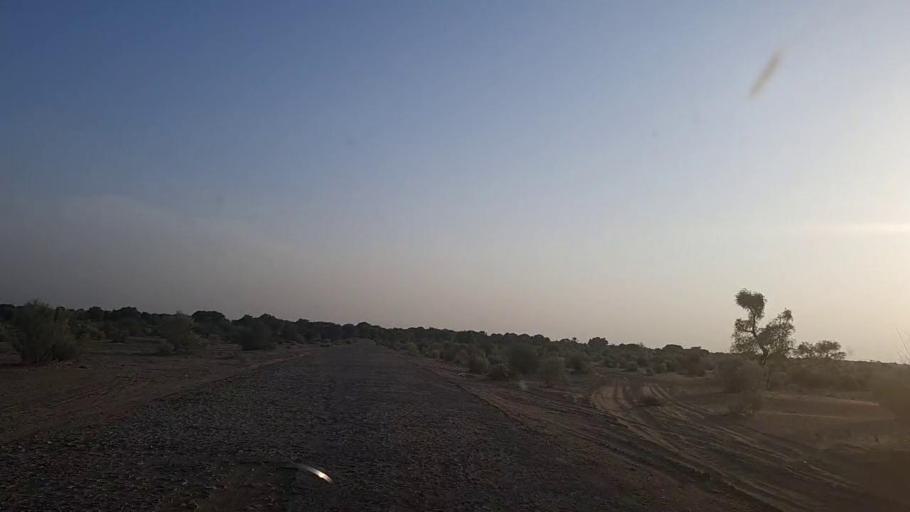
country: PK
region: Sindh
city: Khanpur
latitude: 27.6384
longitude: 69.4515
